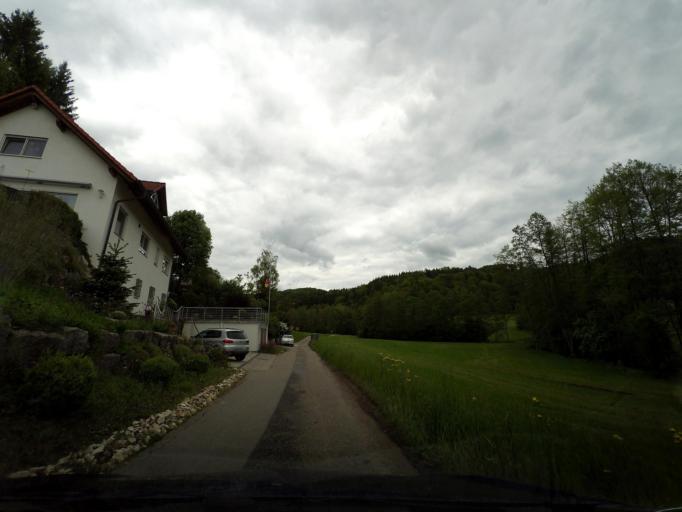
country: DE
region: Baden-Wuerttemberg
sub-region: Regierungsbezirk Stuttgart
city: Murrhardt
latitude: 48.9920
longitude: 9.5549
